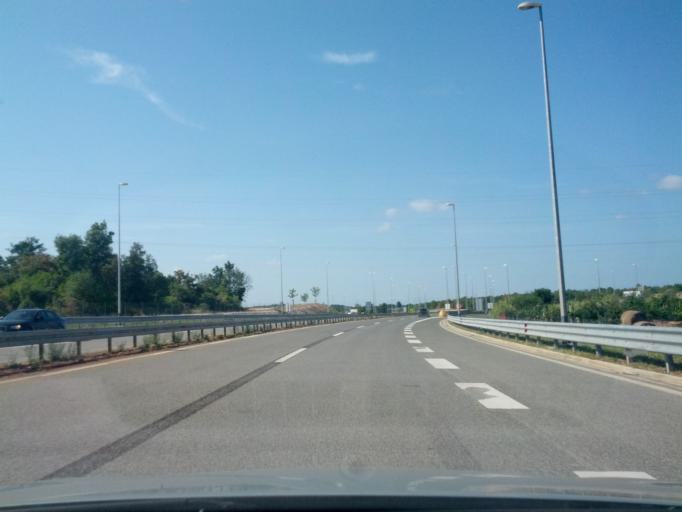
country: HR
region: Istarska
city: Buje
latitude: 45.4420
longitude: 13.6189
